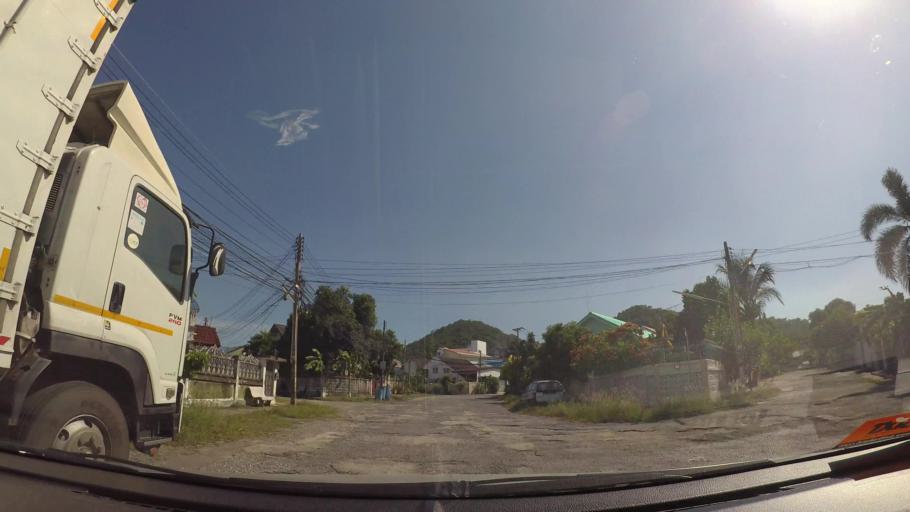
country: TH
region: Chon Buri
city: Si Racha
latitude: 13.1586
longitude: 100.9334
